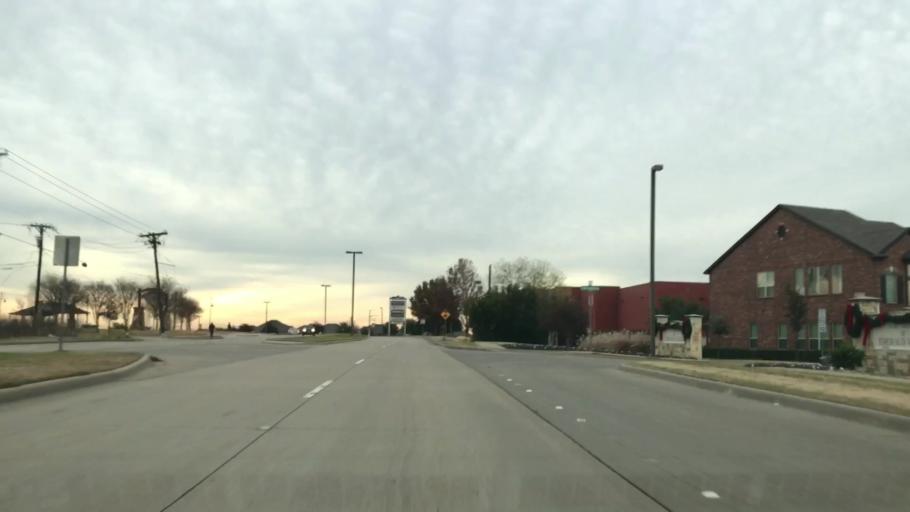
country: US
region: Texas
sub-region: Dallas County
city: Coppell
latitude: 32.9253
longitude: -96.9685
